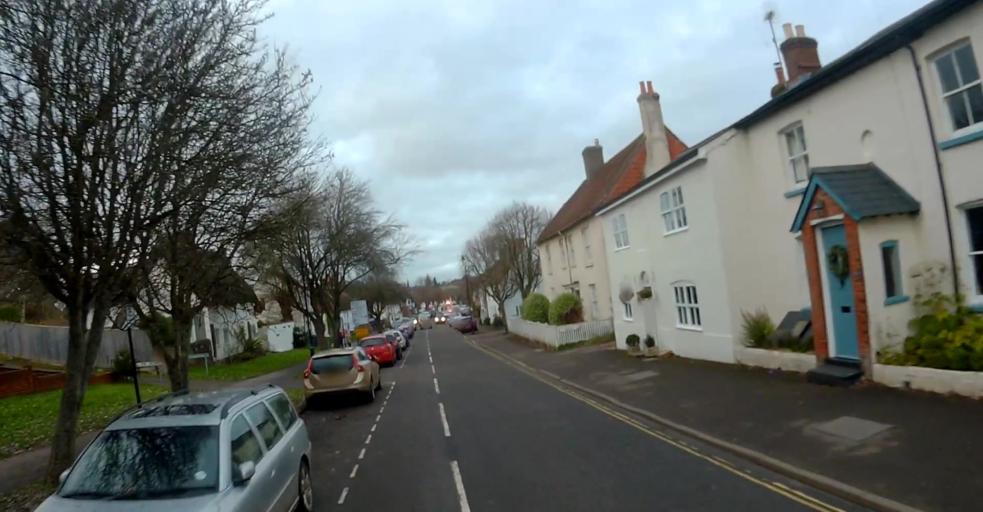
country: GB
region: England
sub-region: Hampshire
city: Overton
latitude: 51.2418
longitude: -1.2626
